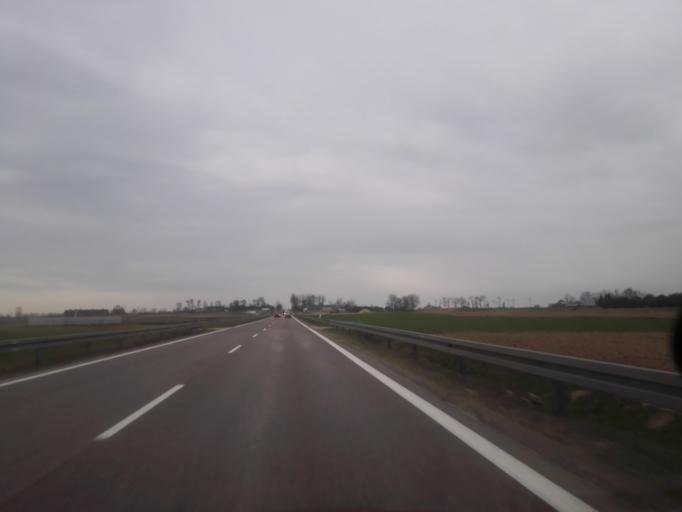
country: PL
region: Podlasie
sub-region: Powiat grajewski
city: Grajewo
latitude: 53.6750
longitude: 22.5824
